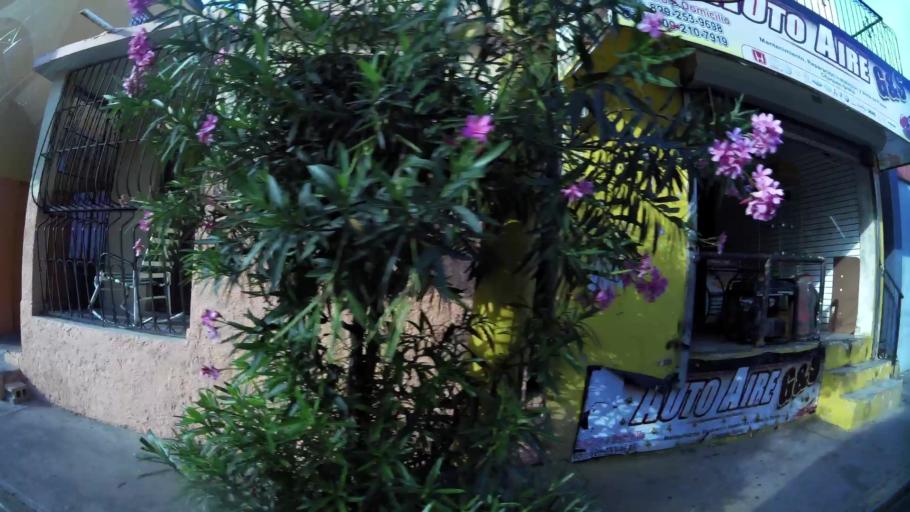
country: DO
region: Santiago
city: Santiago de los Caballeros
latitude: 19.4622
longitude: -70.7101
